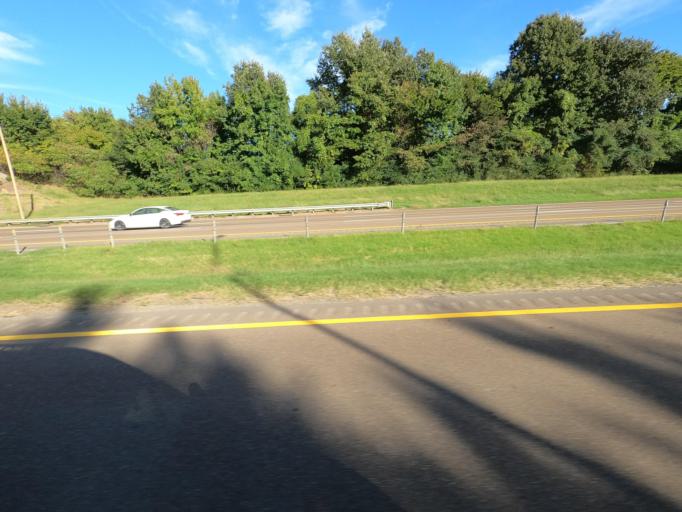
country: US
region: Tennessee
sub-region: Shelby County
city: New South Memphis
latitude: 35.1016
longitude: -90.0763
